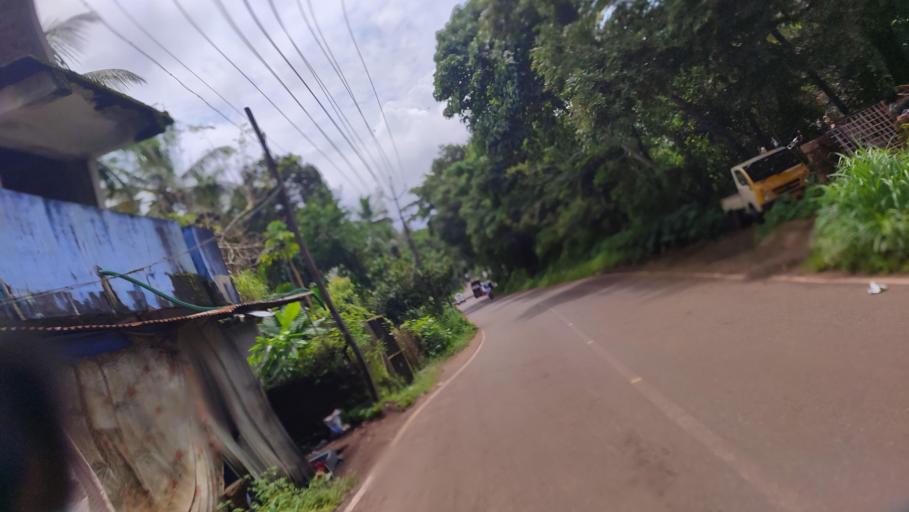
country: IN
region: Kerala
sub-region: Kasaragod District
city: Kannangad
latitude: 12.3915
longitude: 75.0431
